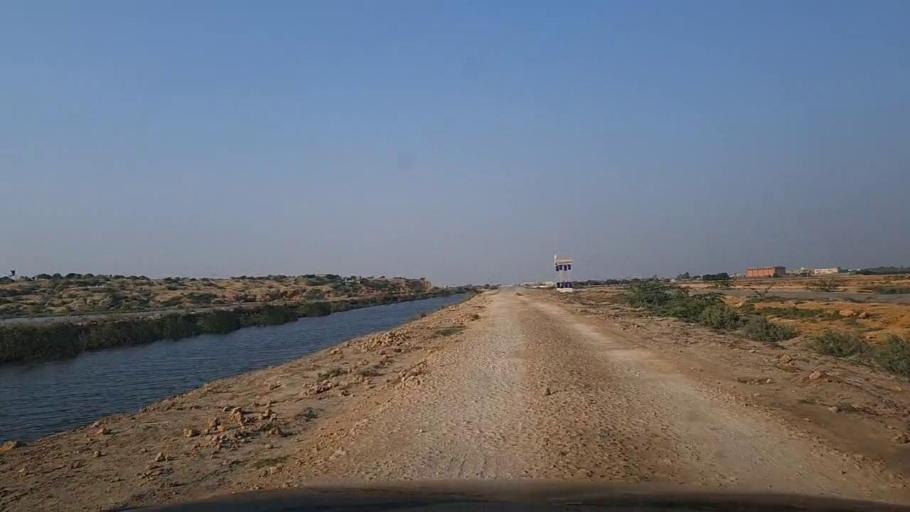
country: PK
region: Sindh
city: Thatta
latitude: 24.7400
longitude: 67.9066
